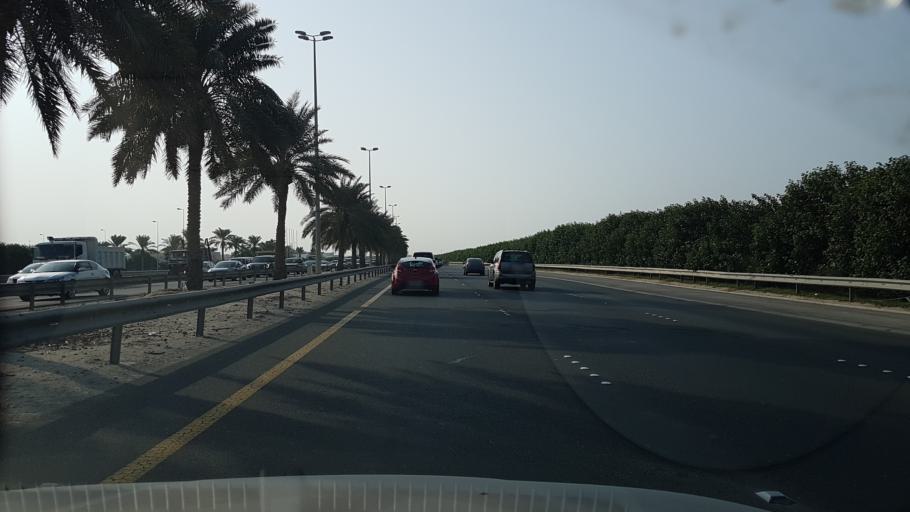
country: BH
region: Northern
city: Madinat `Isa
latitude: 26.1666
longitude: 50.5032
